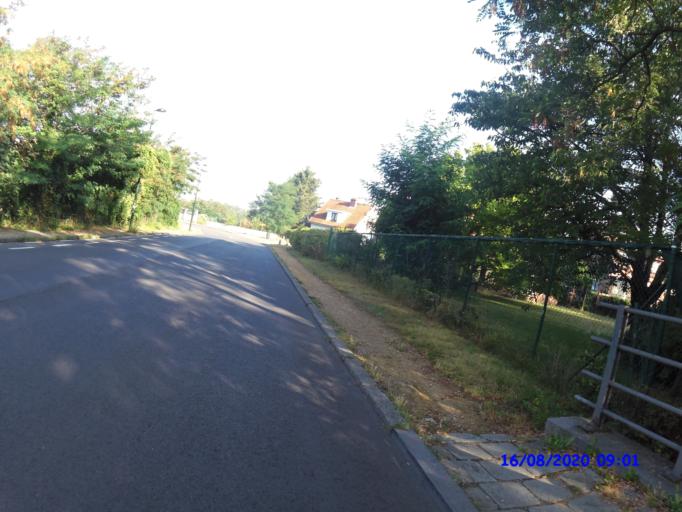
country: BE
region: Flanders
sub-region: Provincie Vlaams-Brabant
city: Linkebeek
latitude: 50.7801
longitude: 4.3345
